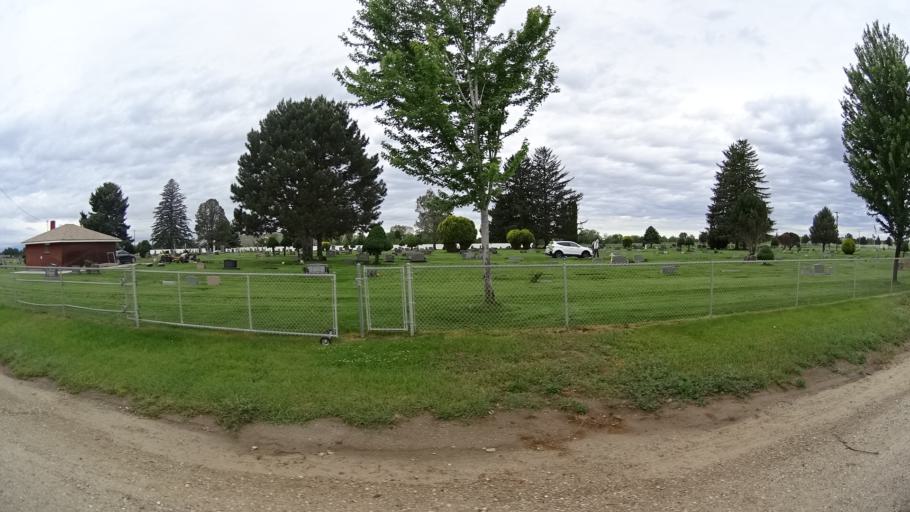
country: US
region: Idaho
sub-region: Ada County
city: Star
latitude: 43.7077
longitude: -116.4684
